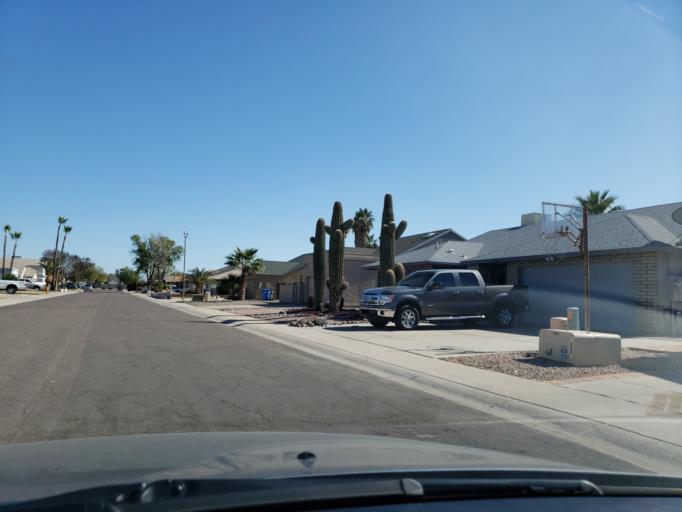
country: US
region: Arizona
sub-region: Maricopa County
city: Glendale
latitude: 33.6501
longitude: -112.0768
